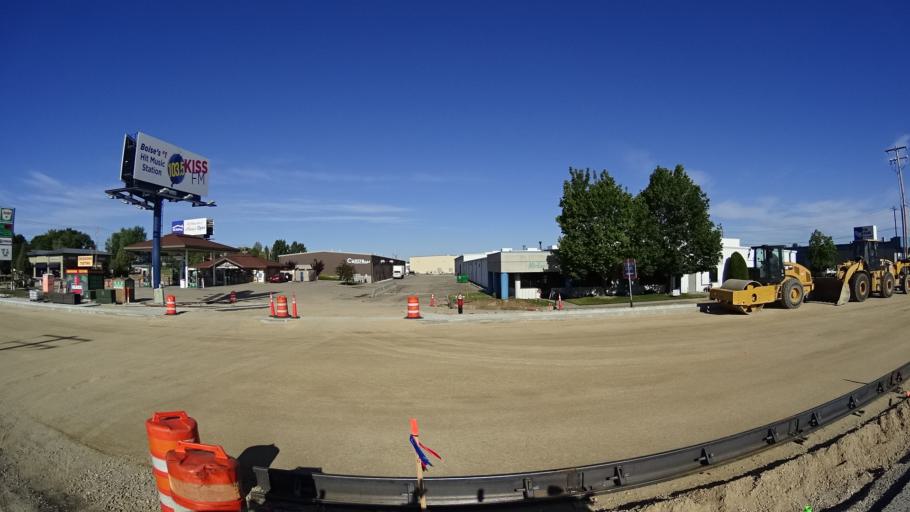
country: US
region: Idaho
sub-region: Ada County
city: Garden City
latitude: 43.5763
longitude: -116.2741
